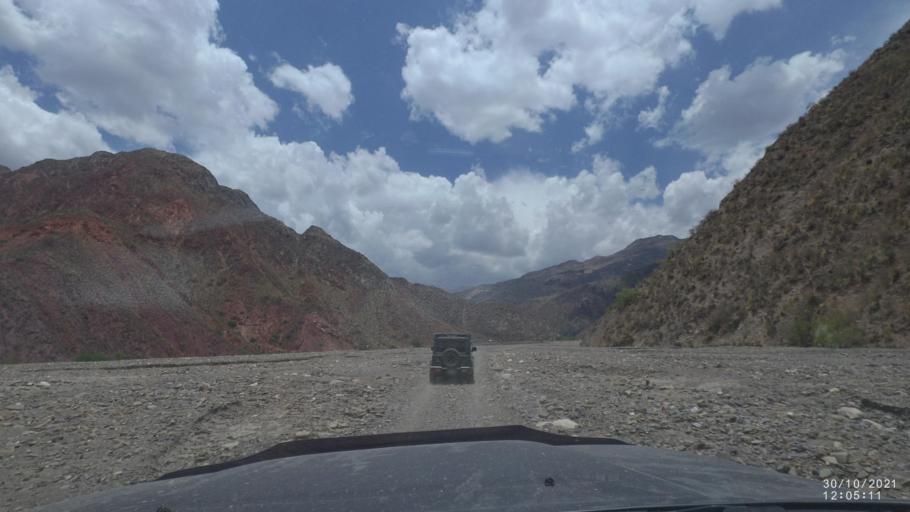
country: BO
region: Cochabamba
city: Colchani
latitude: -17.5335
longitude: -66.6209
